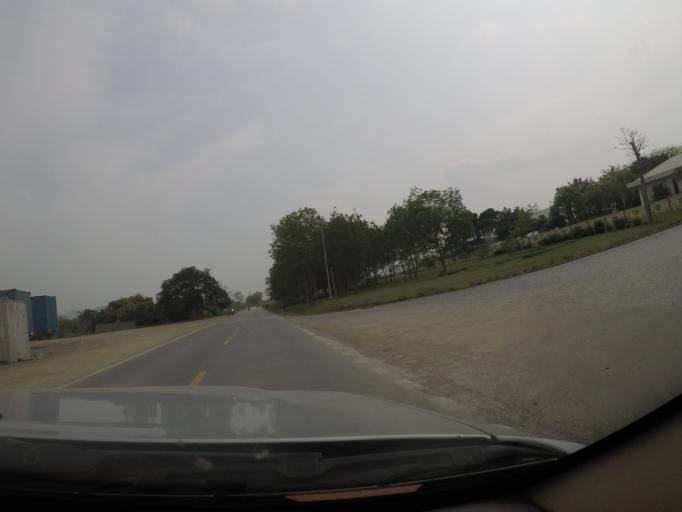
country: VN
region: Nghe An
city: Cau Giat
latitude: 19.3632
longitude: 105.4651
